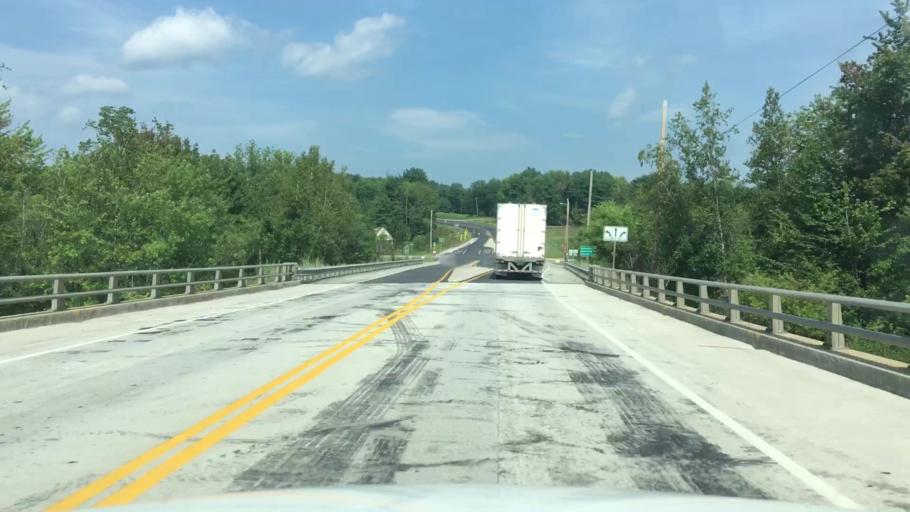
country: US
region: Maine
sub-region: Androscoggin County
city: Turner
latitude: 44.2555
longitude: -70.2591
